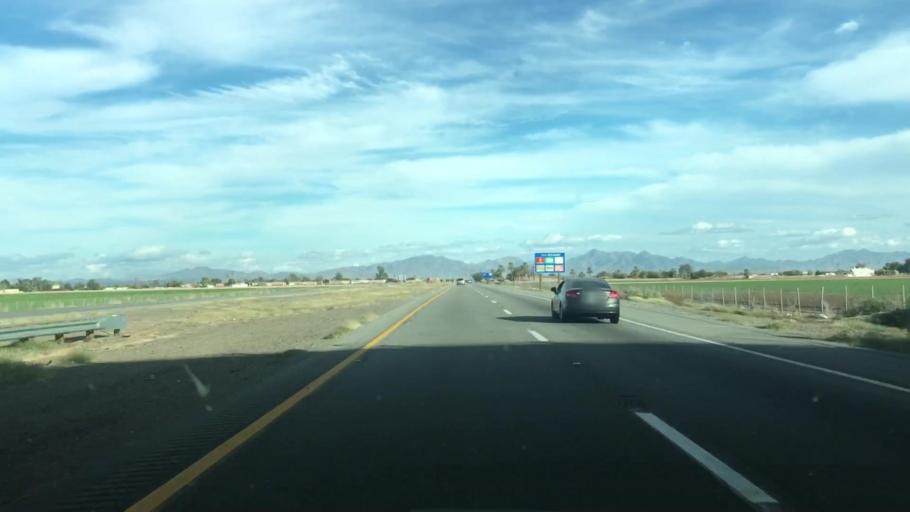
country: US
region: California
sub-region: Riverside County
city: Blythe
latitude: 33.6065
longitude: -114.6400
